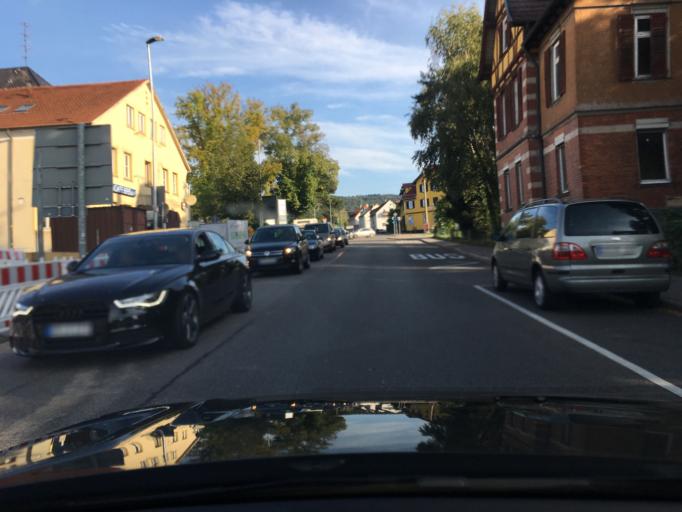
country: DE
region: Baden-Wuerttemberg
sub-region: Regierungsbezirk Stuttgart
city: Schorndorf
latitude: 48.8037
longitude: 9.5347
